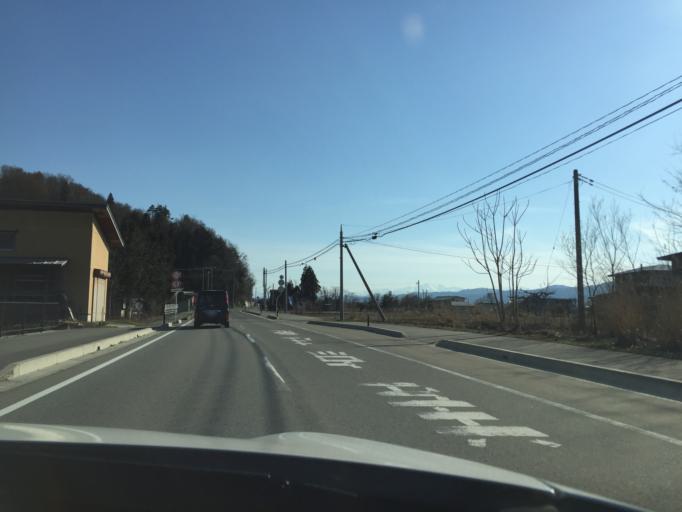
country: JP
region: Yamagata
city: Nagai
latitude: 38.1218
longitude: 140.0536
